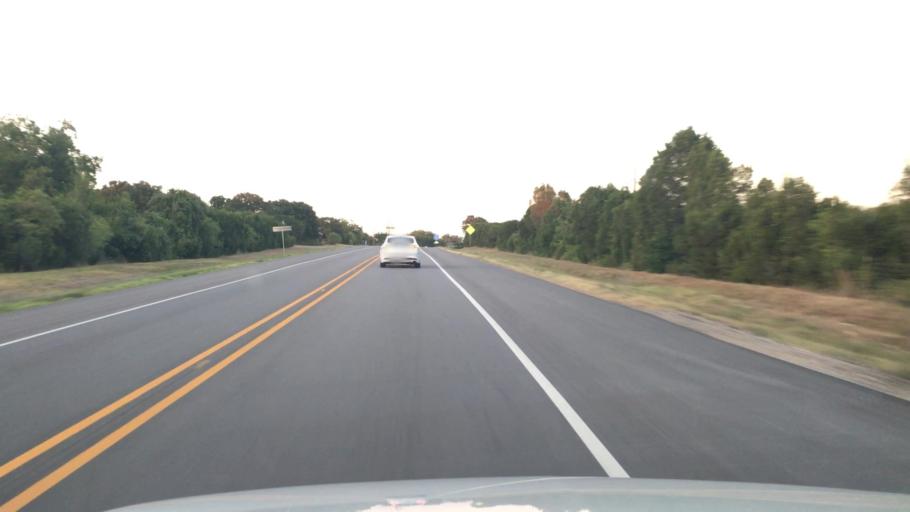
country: US
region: Texas
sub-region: Somervell County
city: Glen Rose
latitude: 32.1956
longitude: -97.8116
